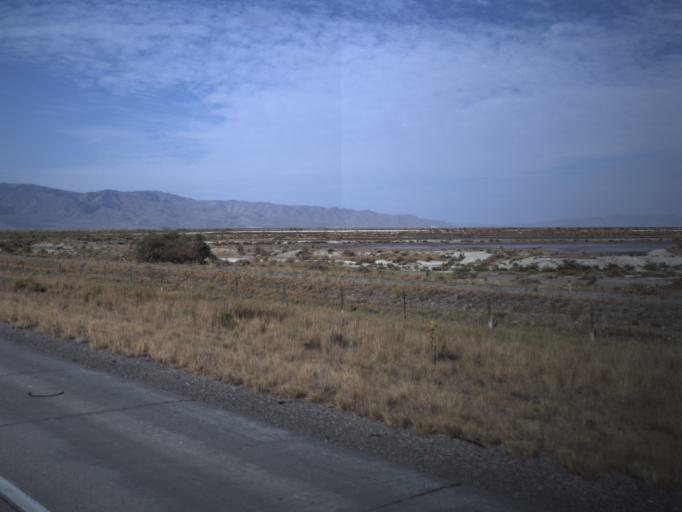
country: US
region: Utah
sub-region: Tooele County
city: Stansbury park
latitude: 40.6713
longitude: -112.2954
